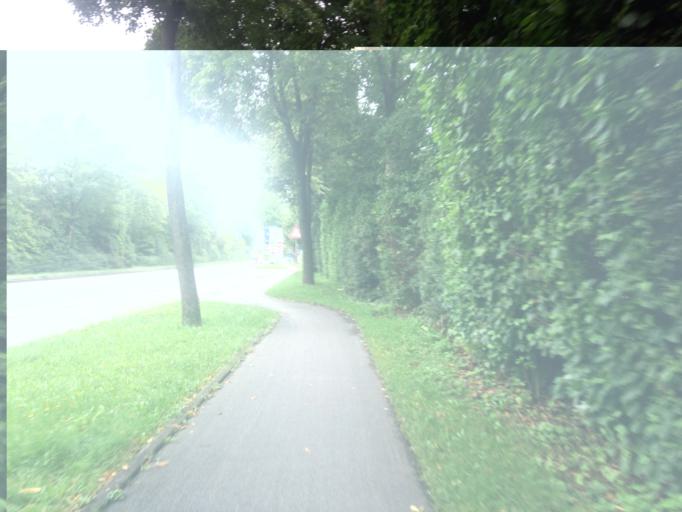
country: DE
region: Bavaria
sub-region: Upper Bavaria
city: Bogenhausen
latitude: 48.1943
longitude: 11.5839
